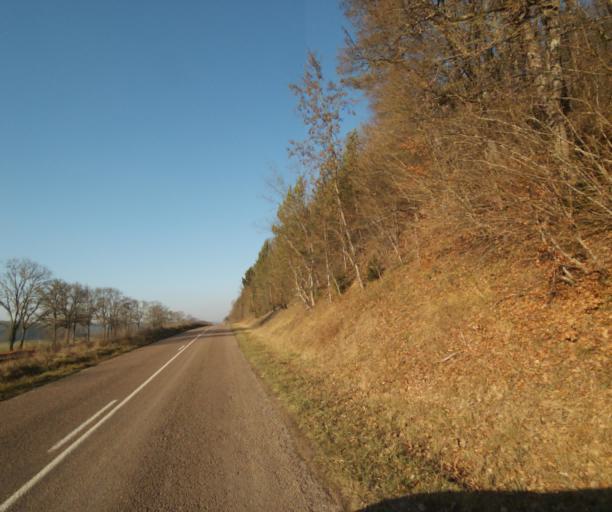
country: FR
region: Champagne-Ardenne
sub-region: Departement de la Haute-Marne
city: Chevillon
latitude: 48.5083
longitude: 5.1234
